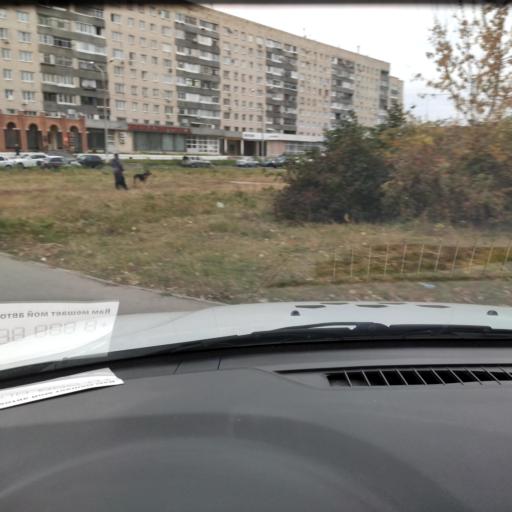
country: RU
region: Samara
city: Tol'yatti
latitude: 53.5042
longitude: 49.4211
